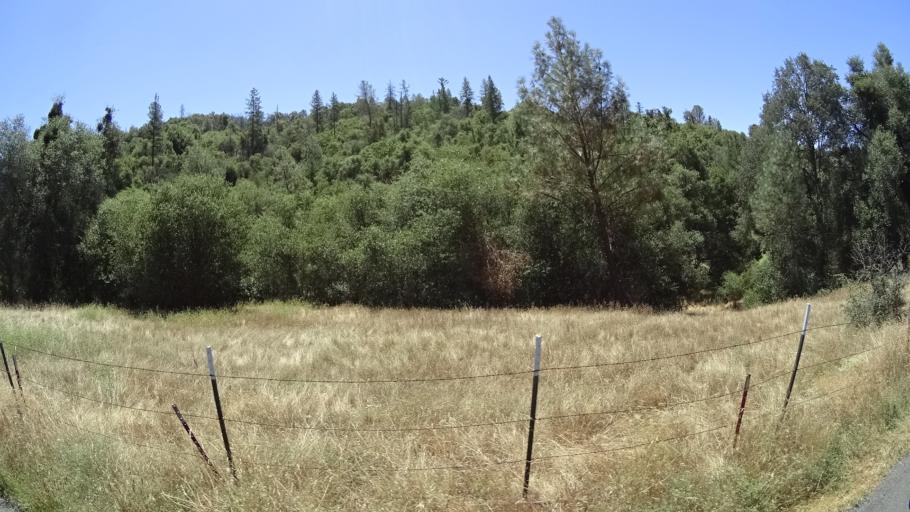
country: US
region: California
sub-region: Calaveras County
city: Mountain Ranch
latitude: 38.1816
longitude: -120.5816
